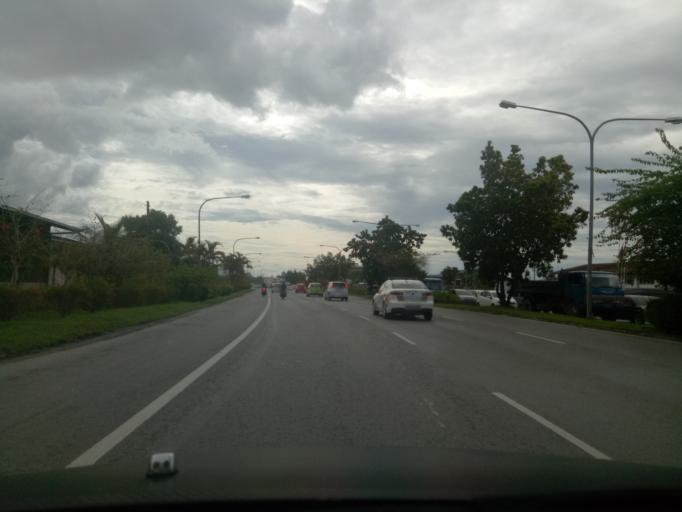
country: MY
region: Sarawak
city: Kuching
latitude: 1.5538
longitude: 110.3855
